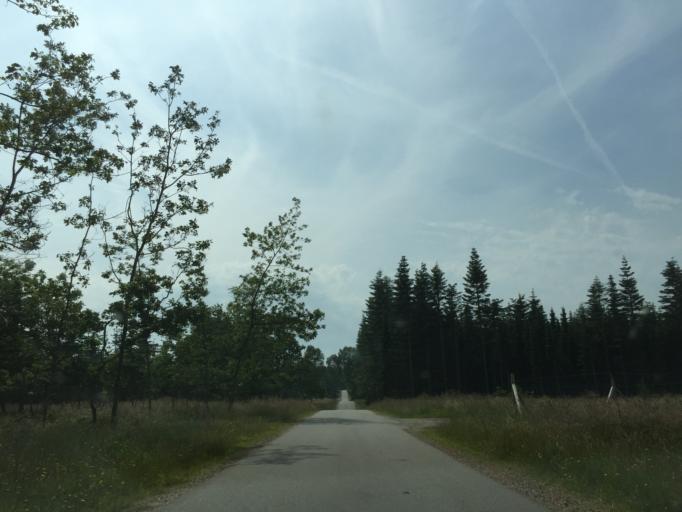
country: DK
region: Central Jutland
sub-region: Silkeborg Kommune
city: Virklund
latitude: 56.0779
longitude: 9.4711
